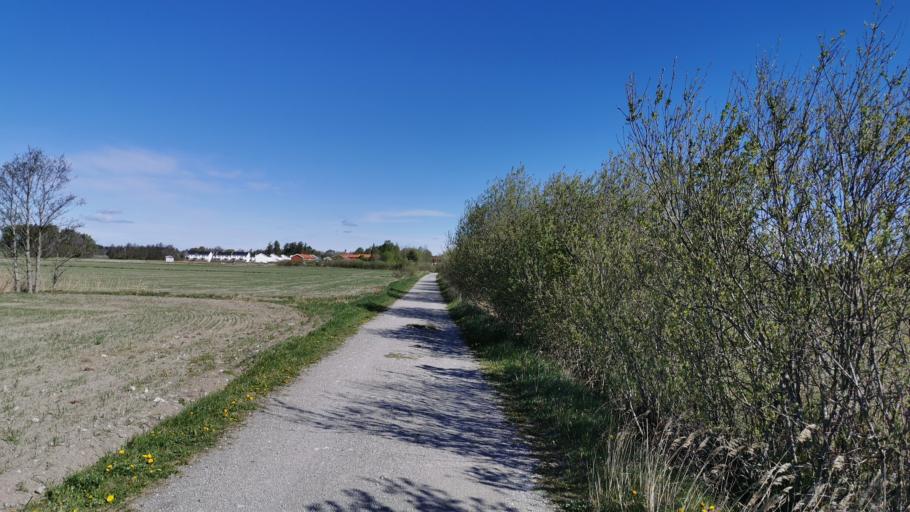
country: SE
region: OErebro
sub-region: Orebro Kommun
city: Orebro
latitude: 59.3090
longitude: 15.2162
